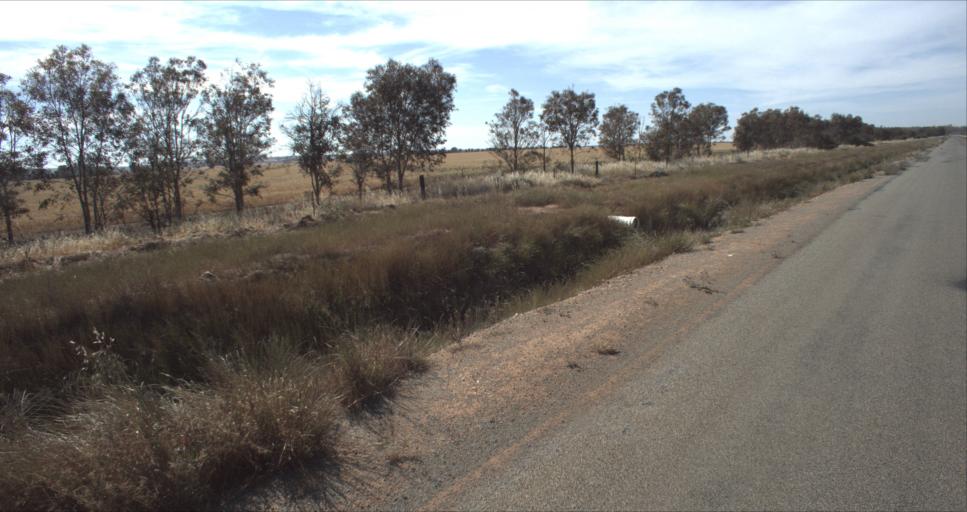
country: AU
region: New South Wales
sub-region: Leeton
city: Leeton
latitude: -34.5621
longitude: 146.4694
